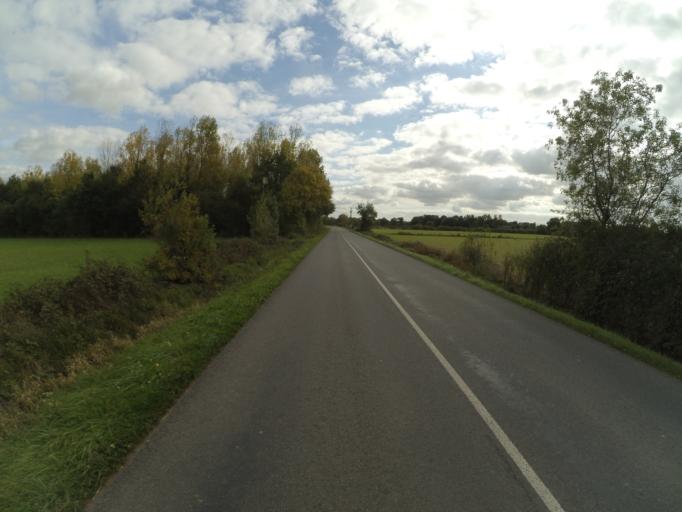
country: FR
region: Pays de la Loire
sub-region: Departement de la Loire-Atlantique
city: Bouvron
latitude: 47.4632
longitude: -1.8349
